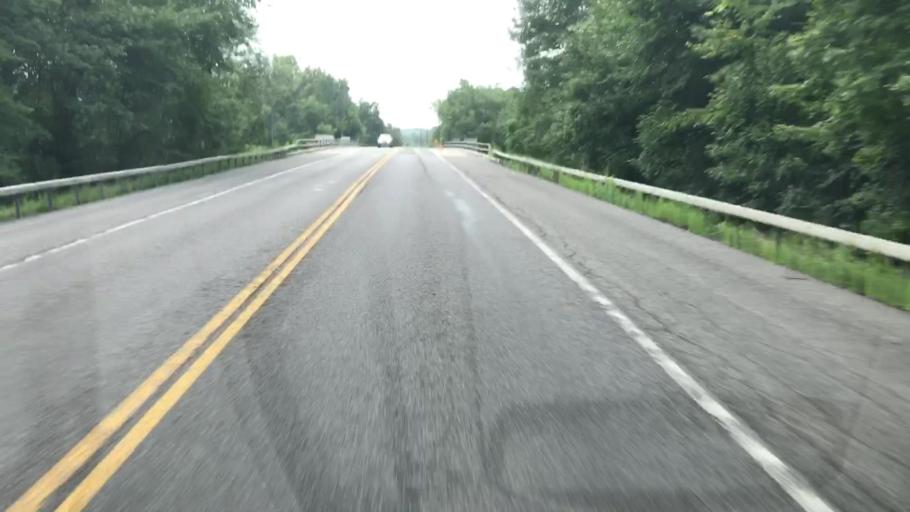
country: US
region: New York
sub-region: Onondaga County
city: Liverpool
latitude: 43.1720
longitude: -76.1987
